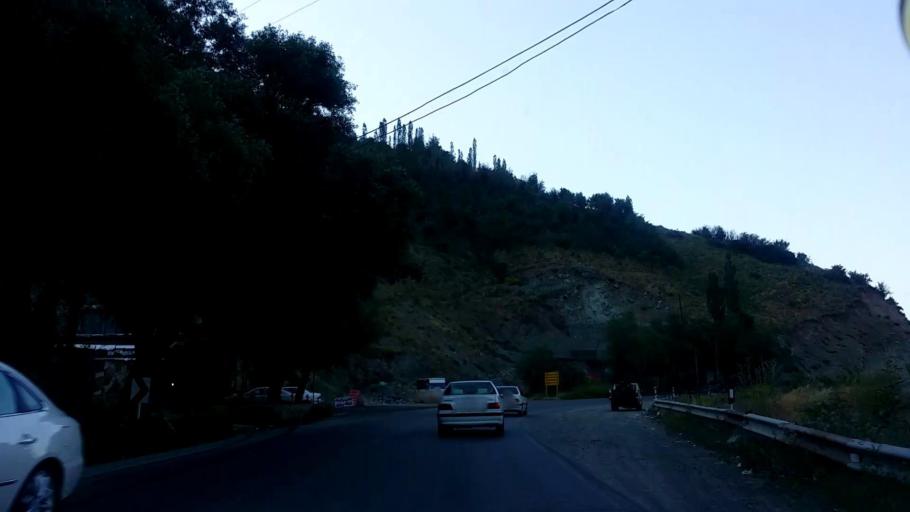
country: IR
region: Tehran
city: Tajrish
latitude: 36.1008
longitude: 51.3155
